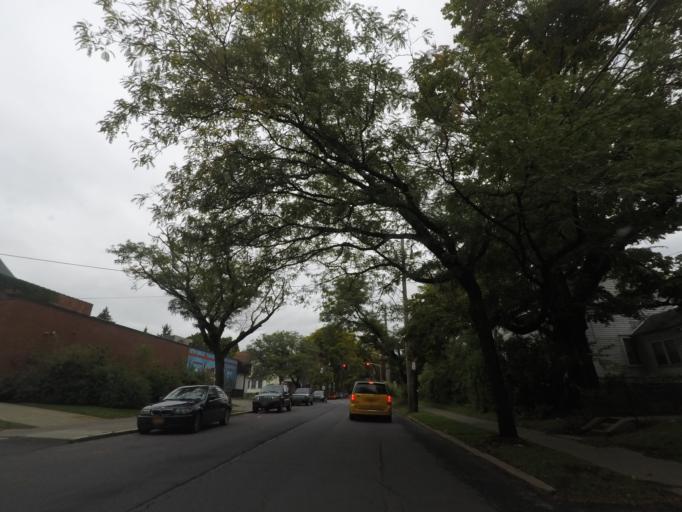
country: US
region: New York
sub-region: Albany County
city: West Albany
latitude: 42.6637
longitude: -73.7896
